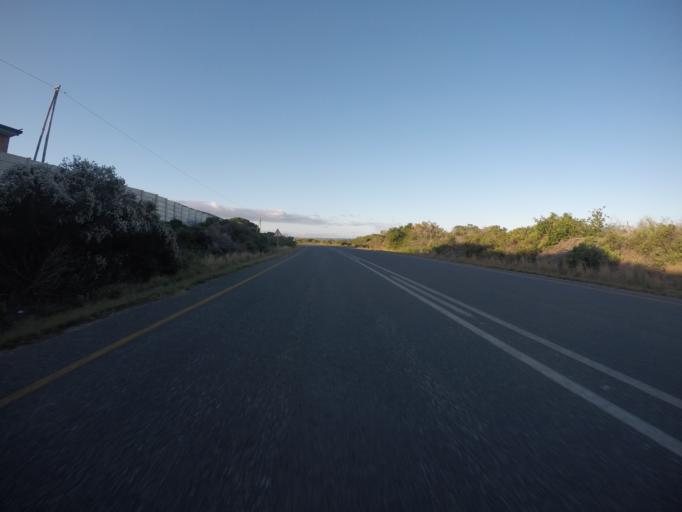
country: ZA
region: Western Cape
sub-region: Eden District Municipality
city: Riversdale
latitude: -34.3869
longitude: 21.4023
